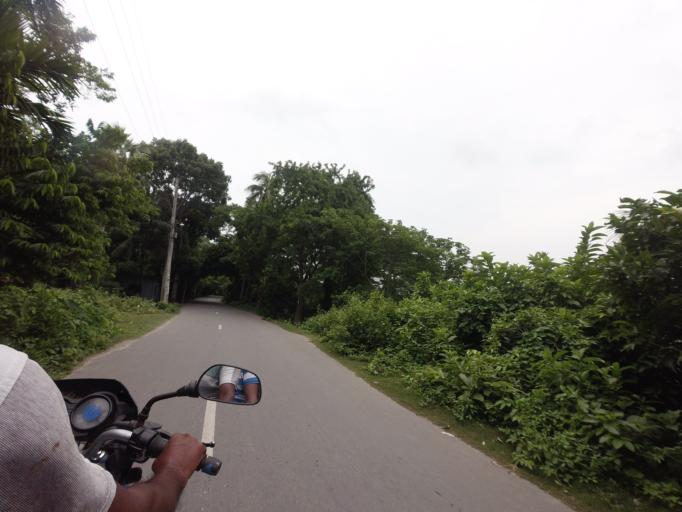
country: BD
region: Khulna
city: Kalia
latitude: 23.1754
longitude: 89.6468
